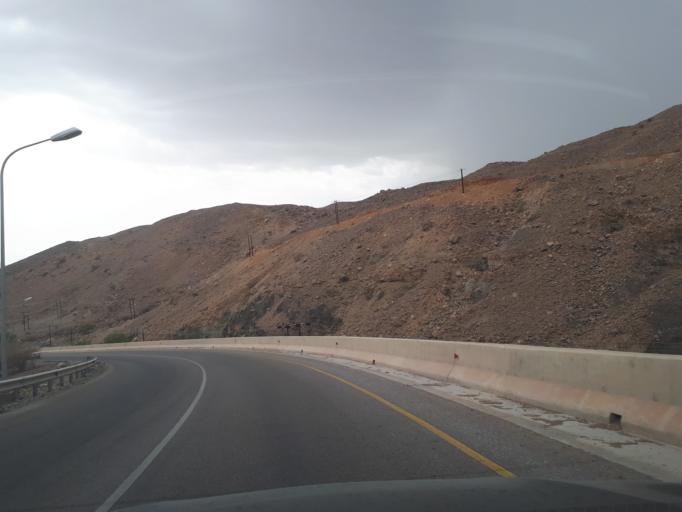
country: OM
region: Ash Sharqiyah
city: Badiyah
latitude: 22.5679
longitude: 59.0606
